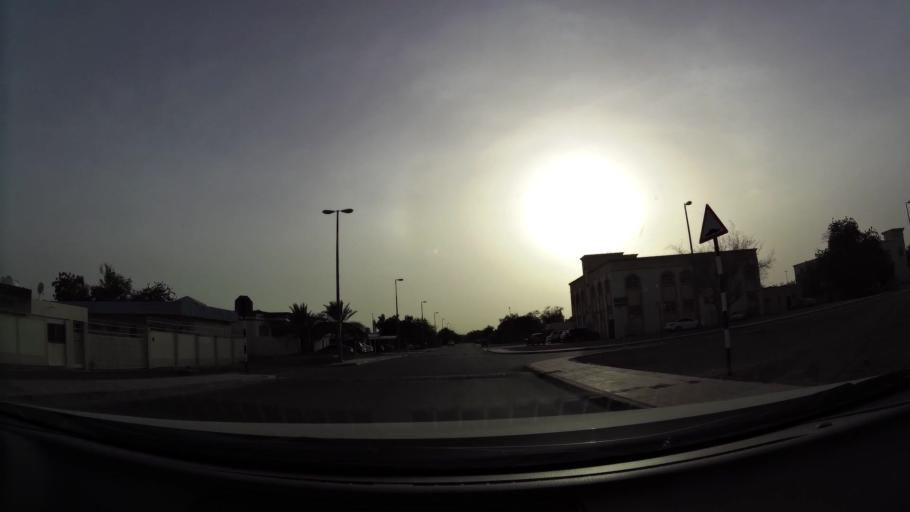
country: OM
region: Al Buraimi
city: Al Buraymi
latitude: 24.2454
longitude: 55.7455
